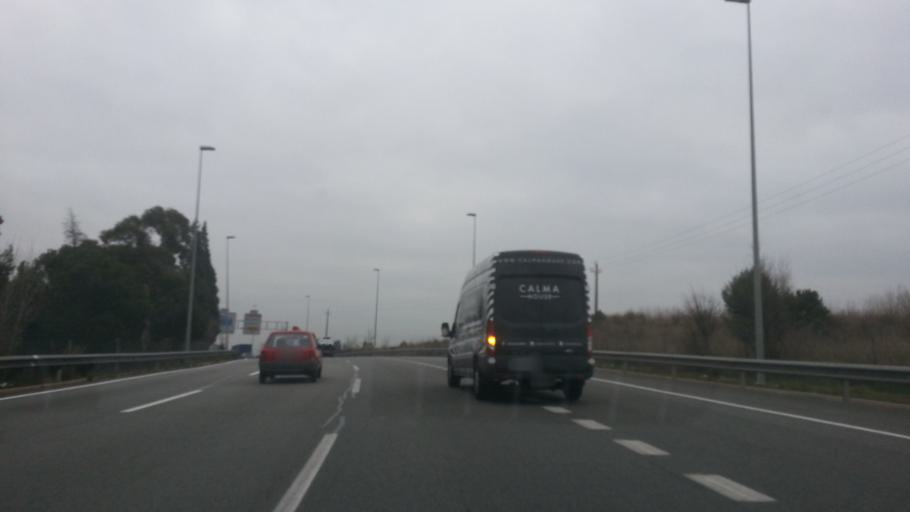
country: ES
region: Catalonia
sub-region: Provincia de Barcelona
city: Sant Cugat del Valles
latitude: 41.4912
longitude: 2.1019
